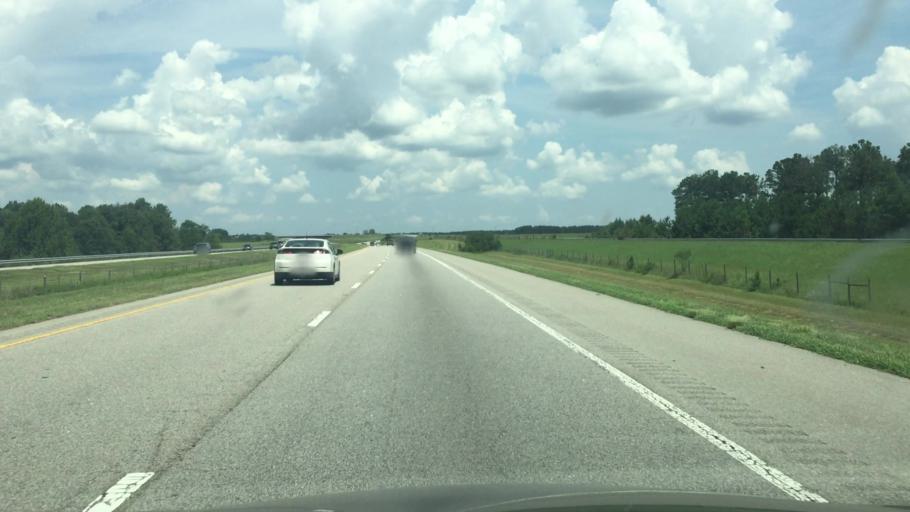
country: US
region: North Carolina
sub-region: Richmond County
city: Ellerbe
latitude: 35.1364
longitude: -79.7140
